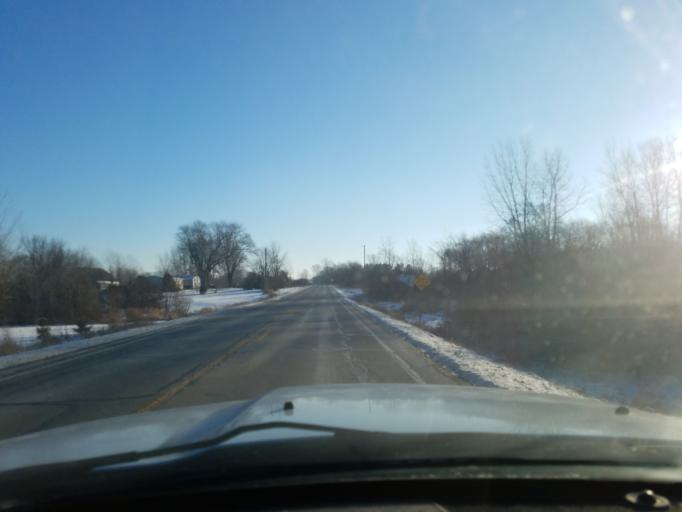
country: US
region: Indiana
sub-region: Noble County
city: Ligonier
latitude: 41.4524
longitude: -85.5561
